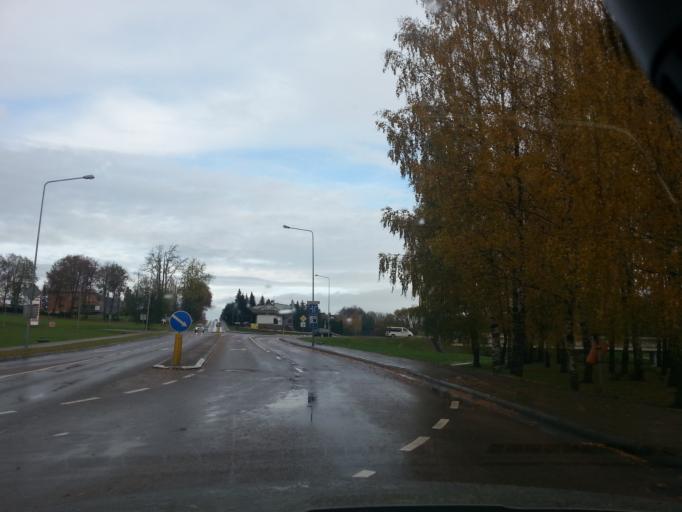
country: LT
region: Marijampoles apskritis
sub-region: Marijampole Municipality
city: Marijampole
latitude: 54.5672
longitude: 23.3402
